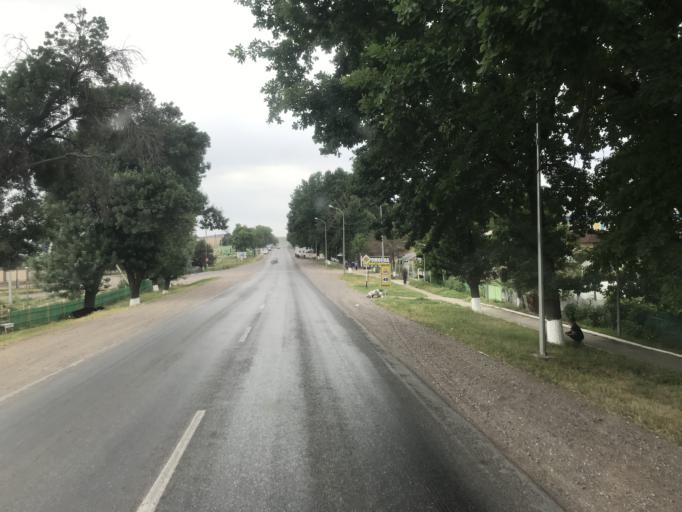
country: KZ
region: Ongtustik Qazaqstan
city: Saryaghash
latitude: 41.4910
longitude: 69.2795
